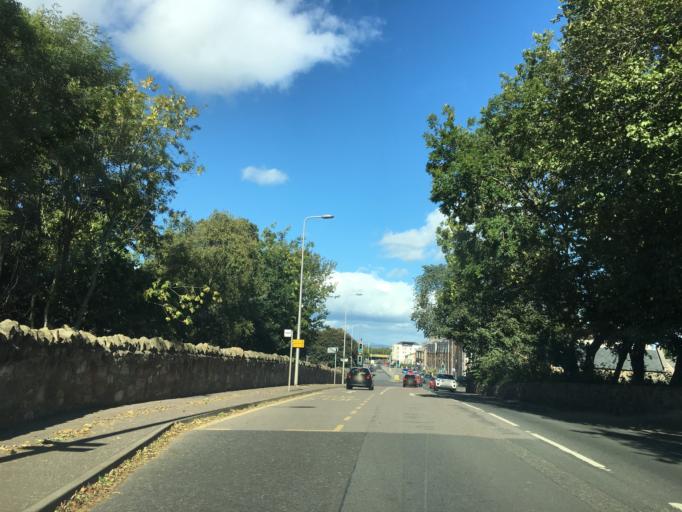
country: GB
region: Scotland
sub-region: West Lothian
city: Seafield
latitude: 55.9328
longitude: -3.1140
